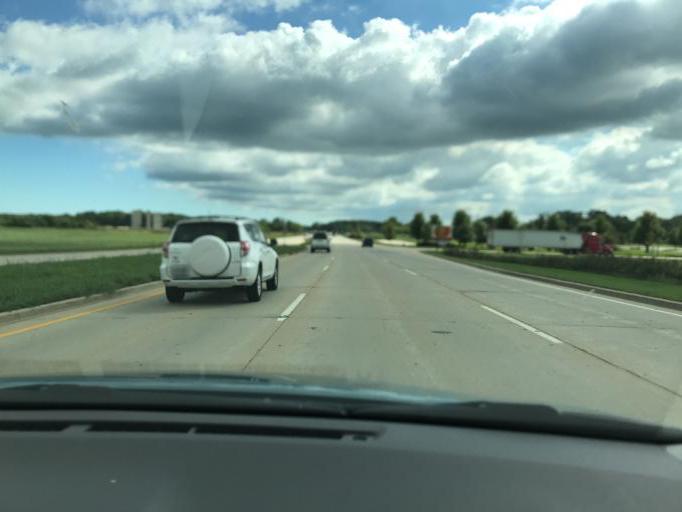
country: US
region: Wisconsin
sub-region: Kenosha County
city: Pleasant Prairie
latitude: 42.5284
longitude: -87.8922
